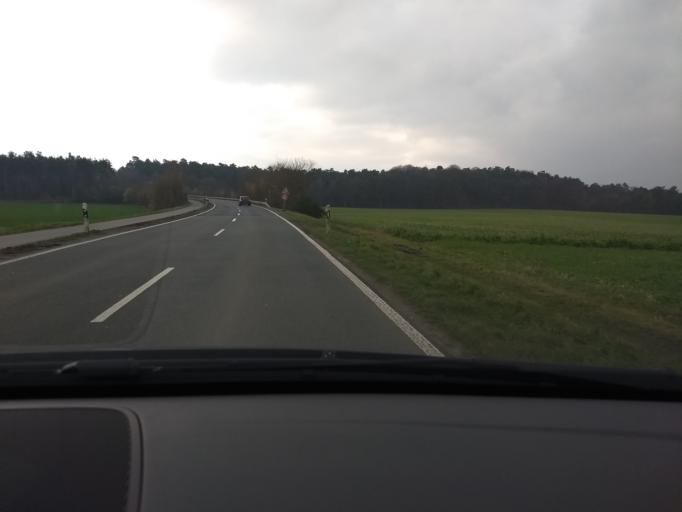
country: DE
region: North Rhine-Westphalia
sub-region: Regierungsbezirk Munster
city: Heiden
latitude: 51.8661
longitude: 6.9186
